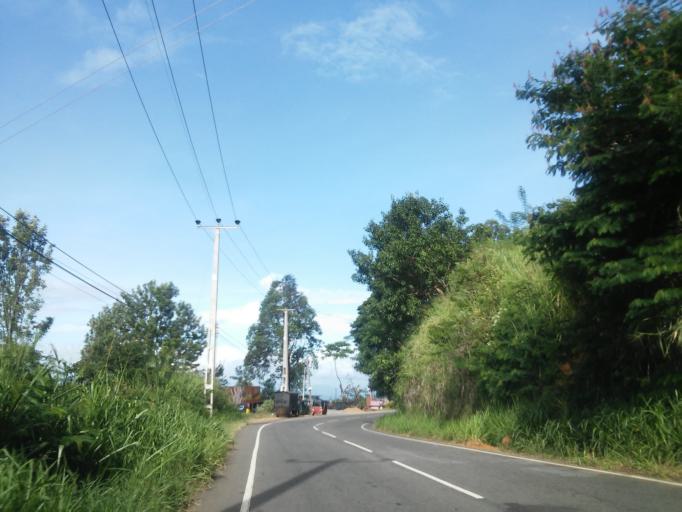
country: LK
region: Uva
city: Haputale
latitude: 6.7630
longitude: 80.9046
